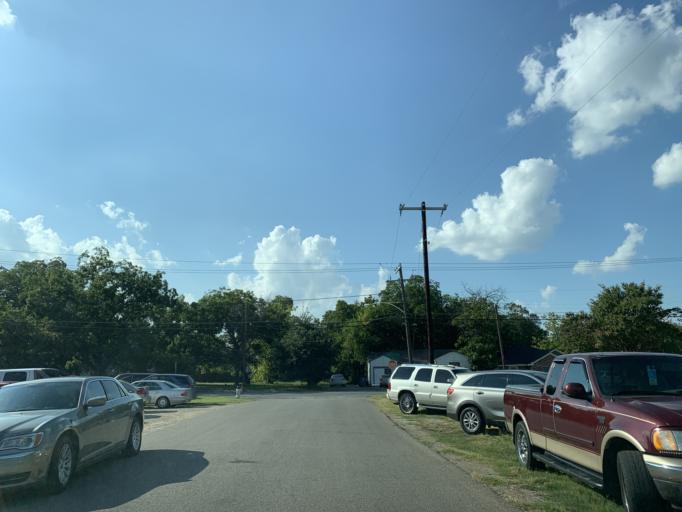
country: US
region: Texas
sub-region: Dallas County
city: Hutchins
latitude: 32.7002
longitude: -96.7795
